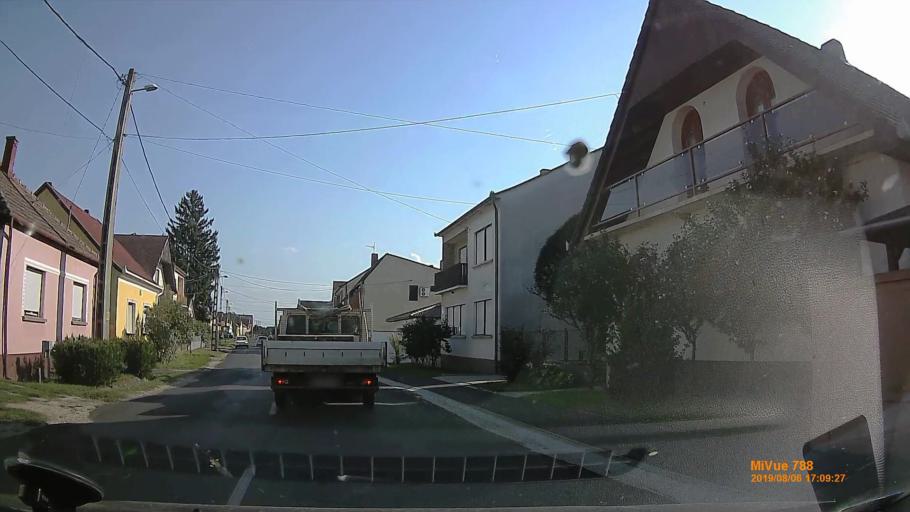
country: HU
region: Zala
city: Nagykanizsa
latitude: 46.4535
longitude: 16.9563
